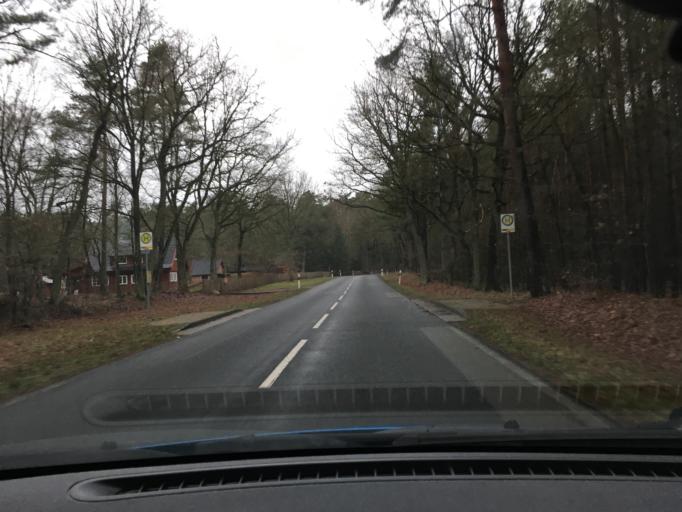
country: DE
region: Mecklenburg-Vorpommern
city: Nostorf
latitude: 53.4158
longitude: 10.6839
